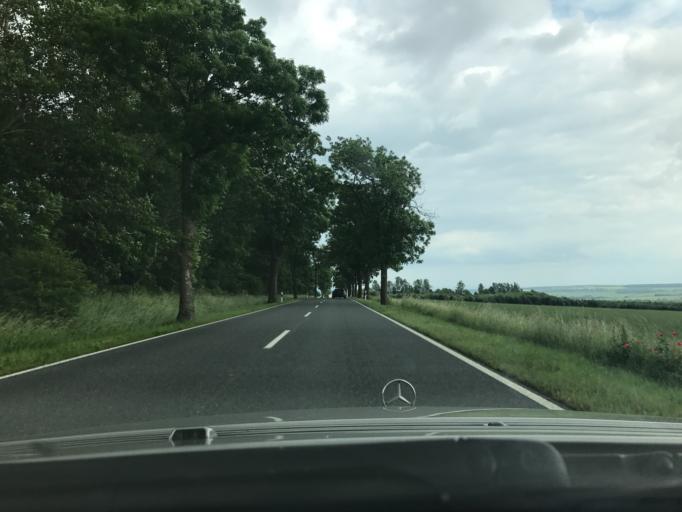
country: DE
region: Thuringia
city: Kefferhausen
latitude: 51.3359
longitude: 10.2761
